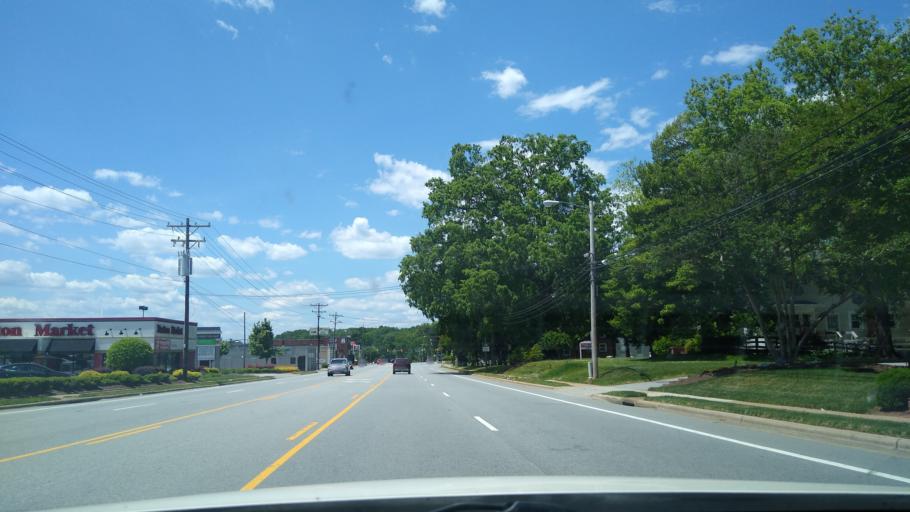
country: US
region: North Carolina
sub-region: Guilford County
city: Greensboro
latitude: 36.0894
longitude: -79.8854
